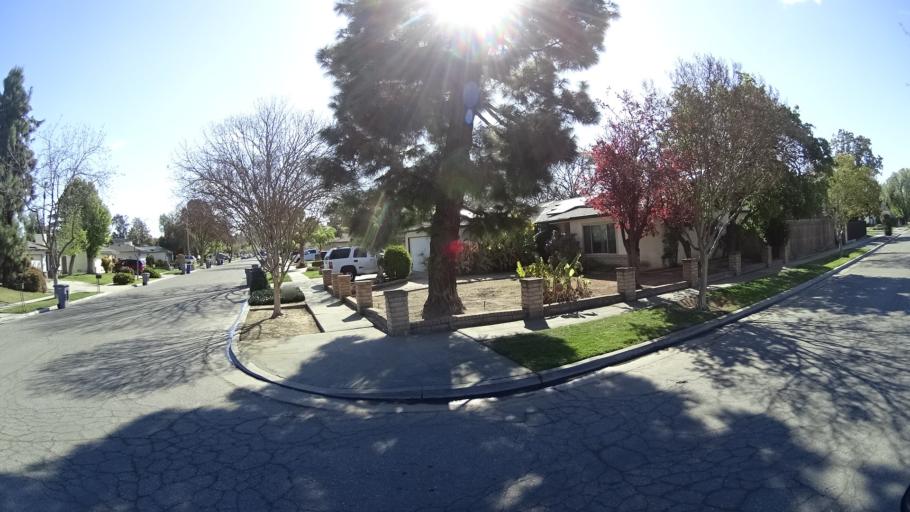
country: US
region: California
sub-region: Fresno County
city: West Park
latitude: 36.8003
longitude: -119.8793
